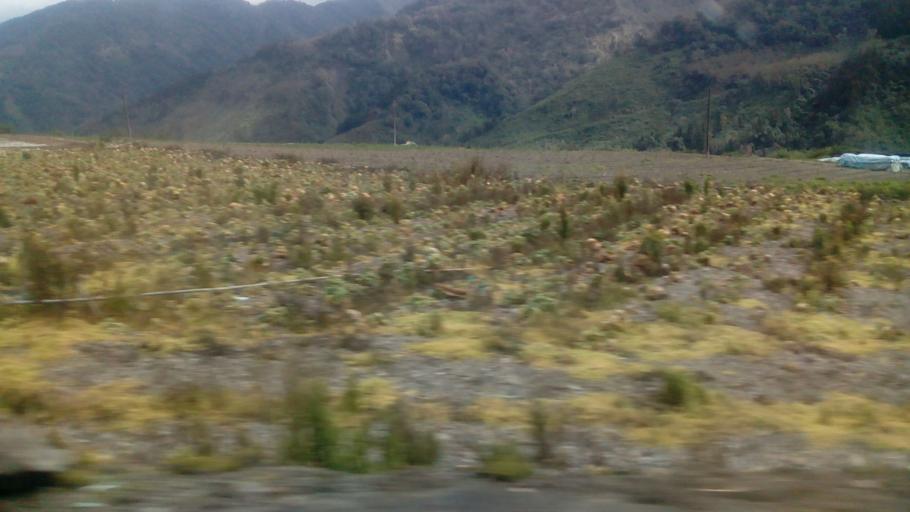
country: TW
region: Taiwan
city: Daxi
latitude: 24.4591
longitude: 121.3942
